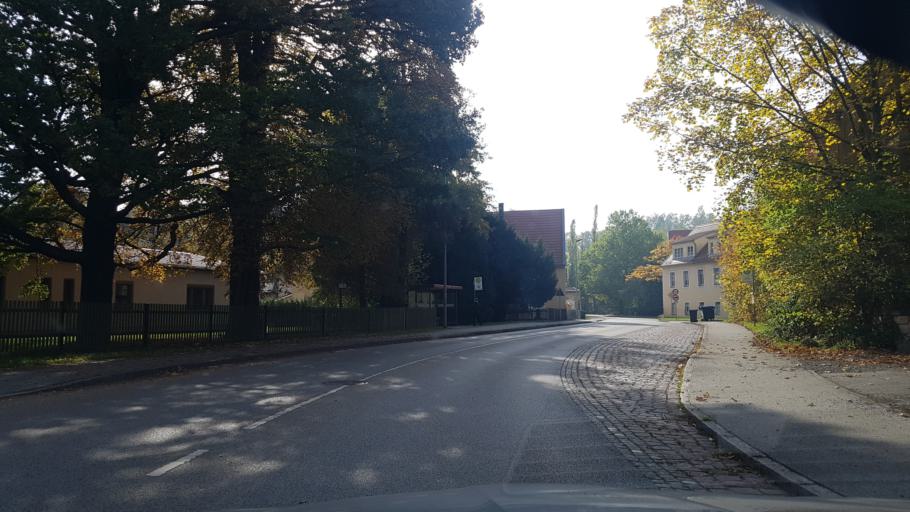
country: DE
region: Saxony
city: Dohma
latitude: 50.9246
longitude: 13.9618
